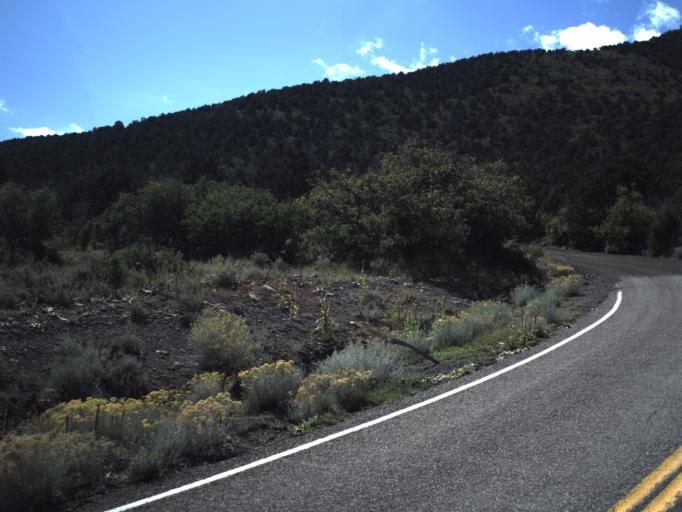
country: US
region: Utah
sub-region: Piute County
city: Junction
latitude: 38.2653
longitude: -112.3046
